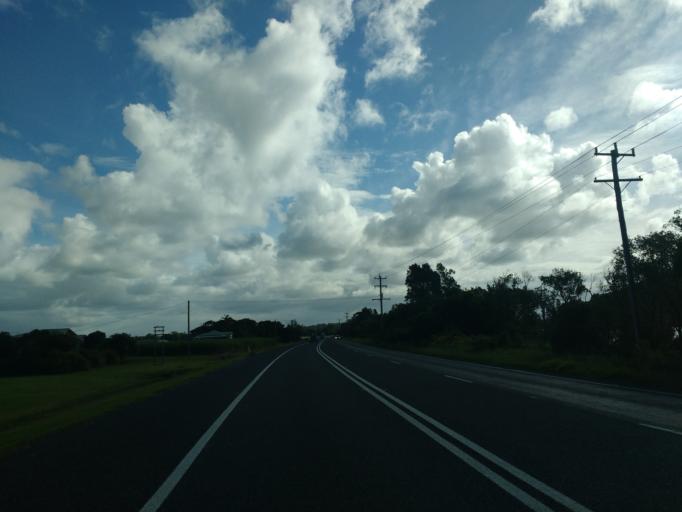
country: AU
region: New South Wales
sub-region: Richmond Valley
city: Evans Head
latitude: -28.9982
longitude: 153.4482
